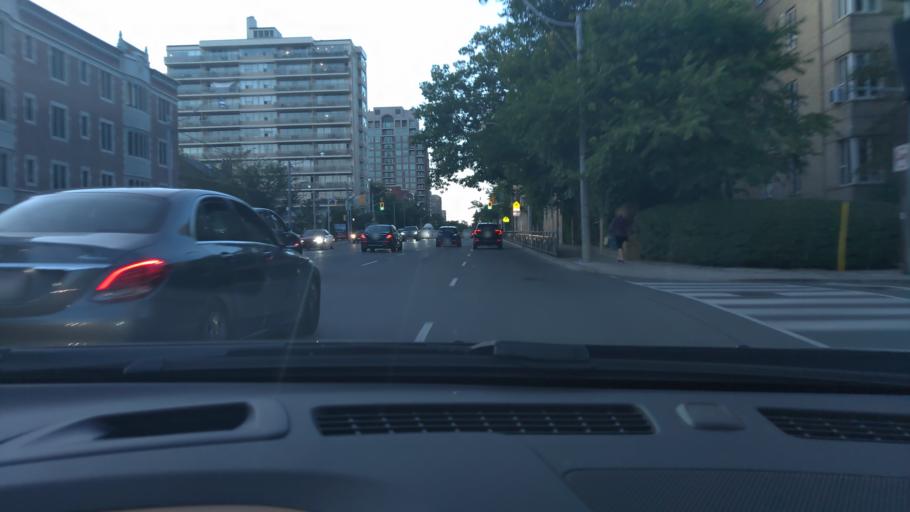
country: CA
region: Ontario
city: Toronto
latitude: 43.6833
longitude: -79.4001
